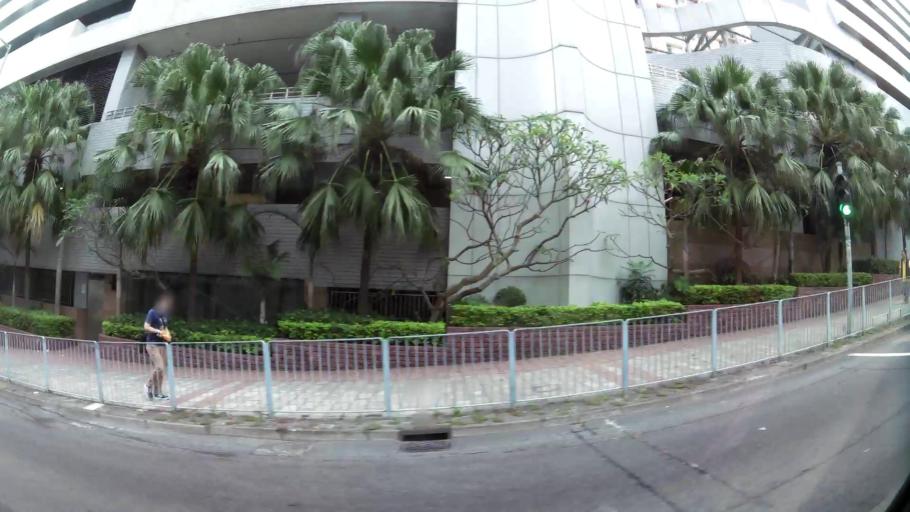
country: HK
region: Kowloon City
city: Kowloon
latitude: 22.3146
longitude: 114.1816
